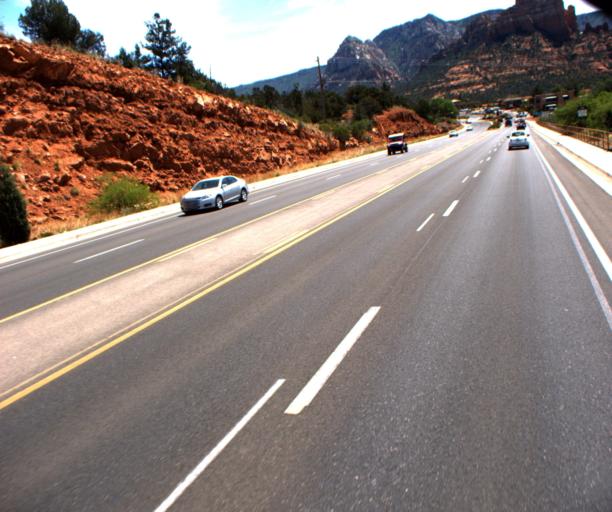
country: US
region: Arizona
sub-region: Coconino County
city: Sedona
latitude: 34.8668
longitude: -111.7678
